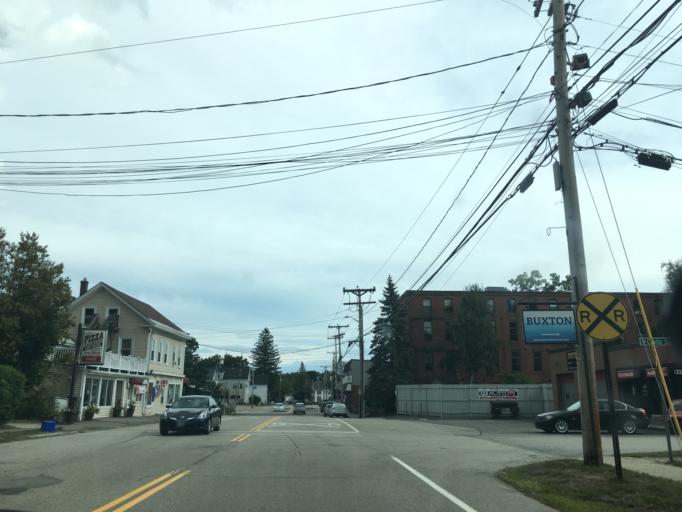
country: US
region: New Hampshire
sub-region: Rockingham County
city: Exeter
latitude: 42.9791
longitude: -70.9619
